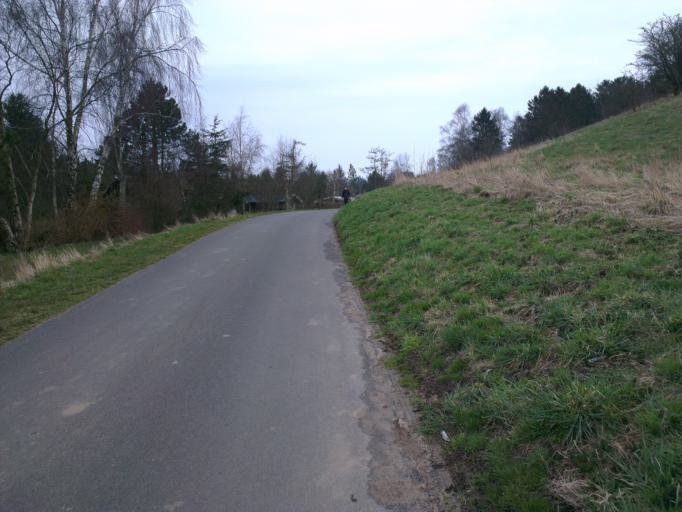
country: DK
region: Zealand
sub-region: Lejre Kommune
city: Ejby
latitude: 55.7394
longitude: 11.8677
